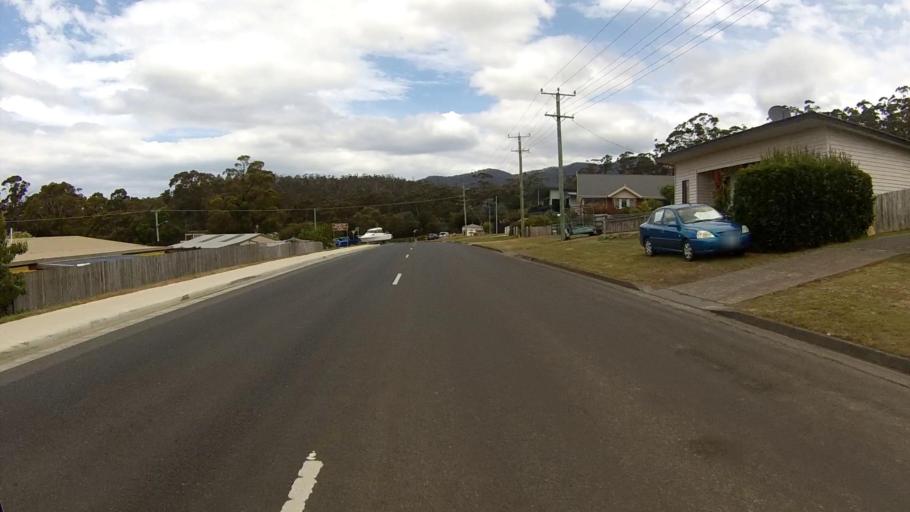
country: AU
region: Tasmania
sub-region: Sorell
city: Sorell
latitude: -42.5655
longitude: 147.8735
